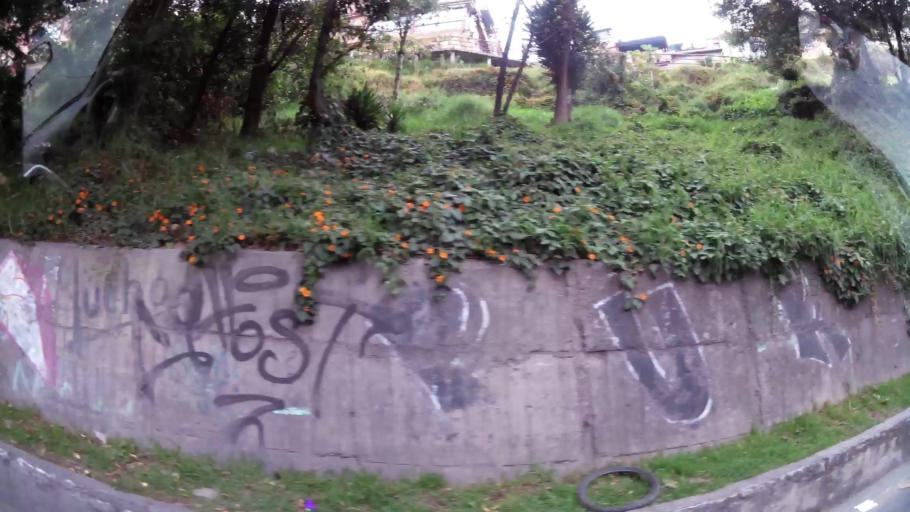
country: CO
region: Cundinamarca
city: La Calera
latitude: 4.7674
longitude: -74.0265
